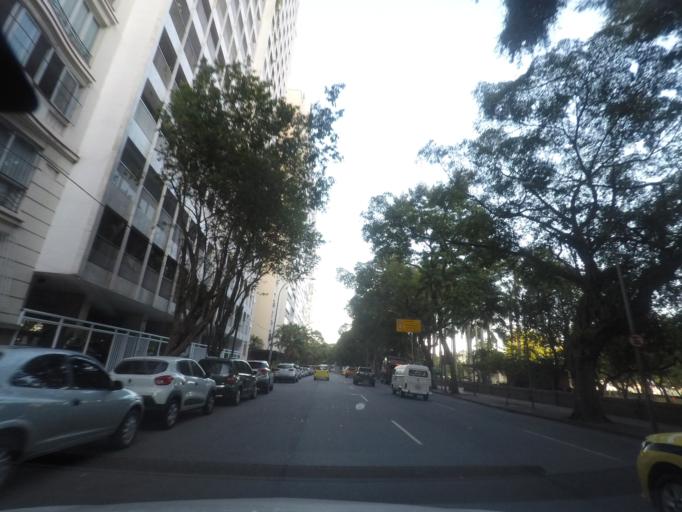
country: BR
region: Rio de Janeiro
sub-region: Rio De Janeiro
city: Rio de Janeiro
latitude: -22.9418
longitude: -43.1733
